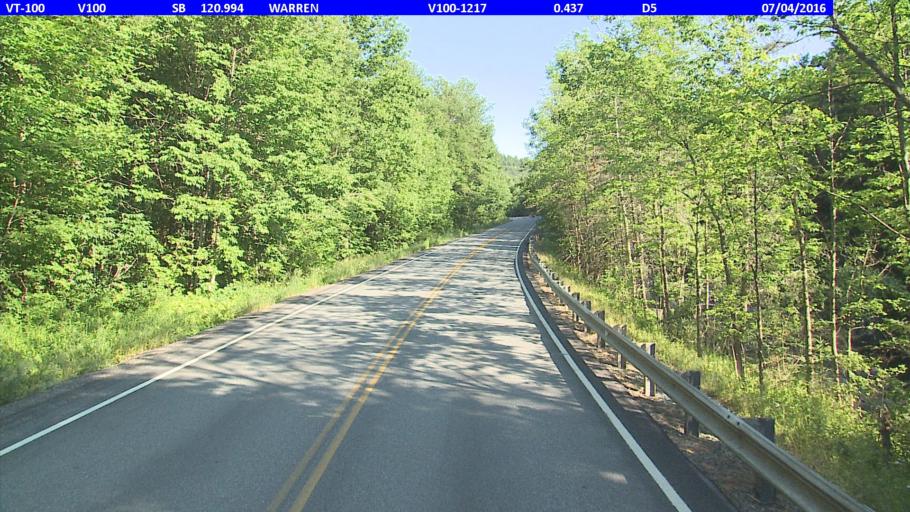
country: US
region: Vermont
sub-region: Washington County
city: Northfield
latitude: 44.0663
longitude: -72.8569
